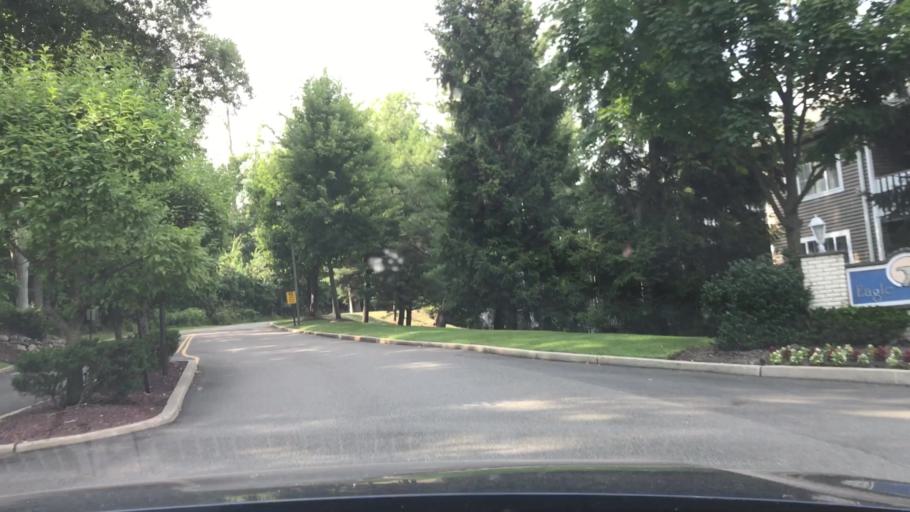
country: US
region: New York
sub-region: Rockland County
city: Spring Valley
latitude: 41.1115
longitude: -74.0216
